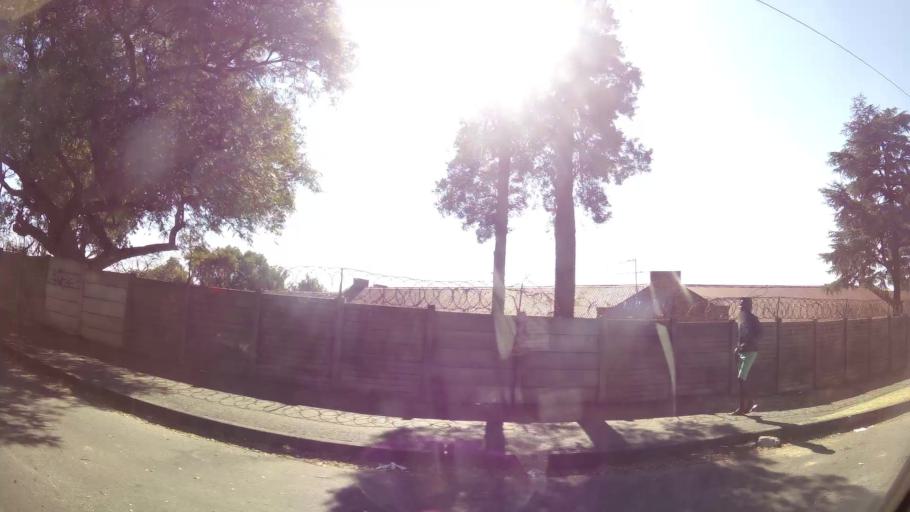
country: ZA
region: Gauteng
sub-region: City of Johannesburg Metropolitan Municipality
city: Johannesburg
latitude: -26.2433
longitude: 28.0891
